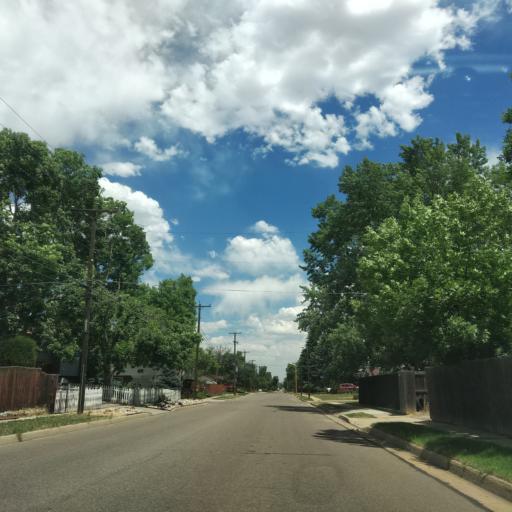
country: US
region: Colorado
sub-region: Jefferson County
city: Lakewood
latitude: 39.6894
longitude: -105.0945
